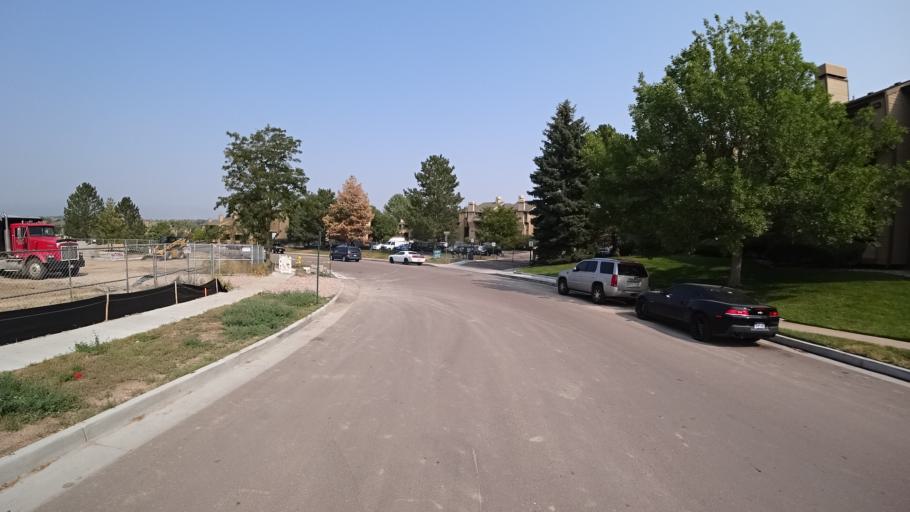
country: US
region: Colorado
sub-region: El Paso County
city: Stratmoor
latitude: 38.8155
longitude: -104.7638
